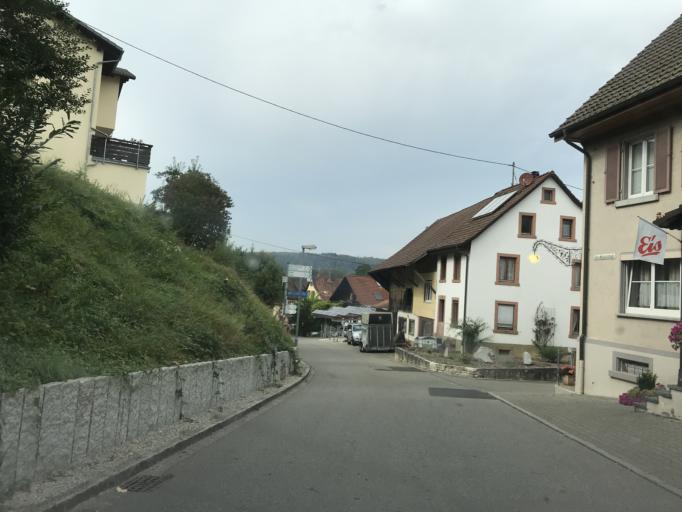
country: DE
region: Baden-Wuerttemberg
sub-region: Freiburg Region
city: Schopfheim
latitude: 47.6455
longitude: 7.8459
